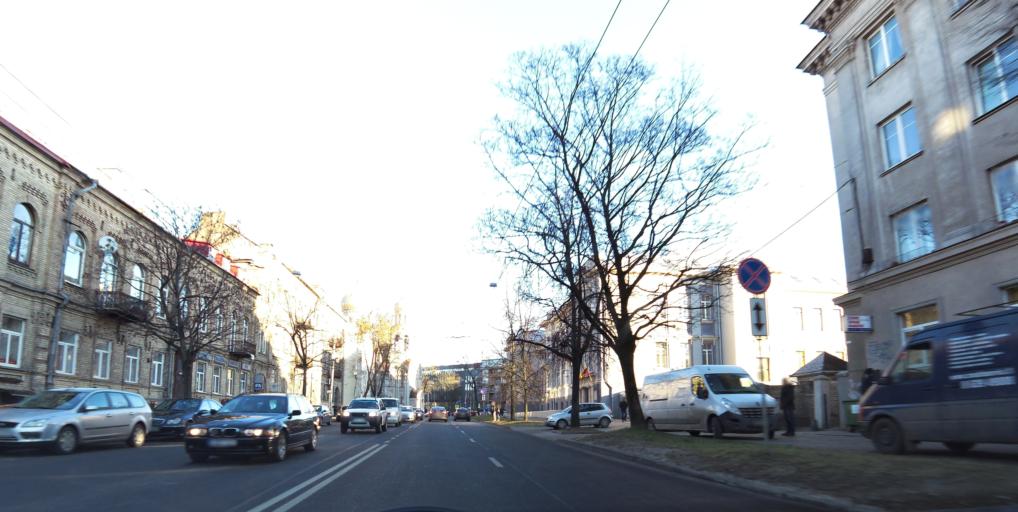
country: LT
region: Vilnius County
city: Naujamiestis
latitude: 54.6816
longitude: 25.2665
